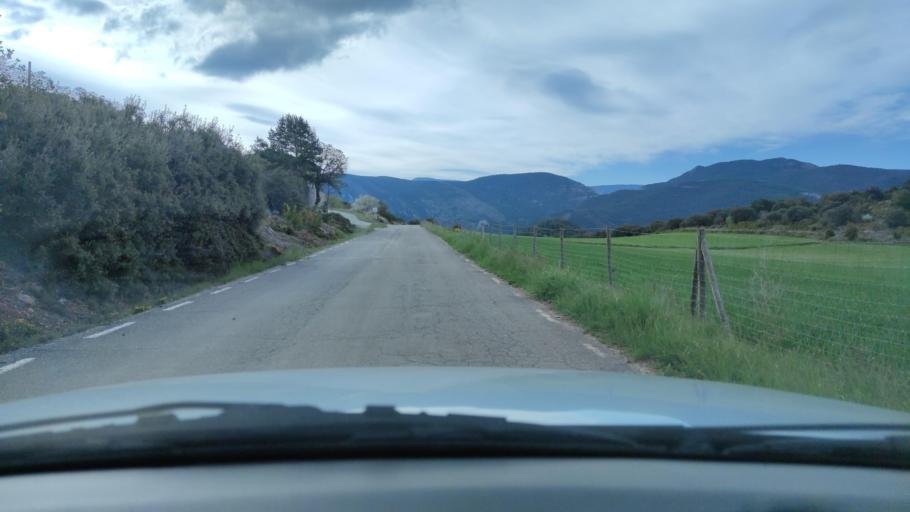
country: ES
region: Catalonia
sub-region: Provincia de Lleida
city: Coll de Nargo
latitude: 42.2391
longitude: 1.3794
